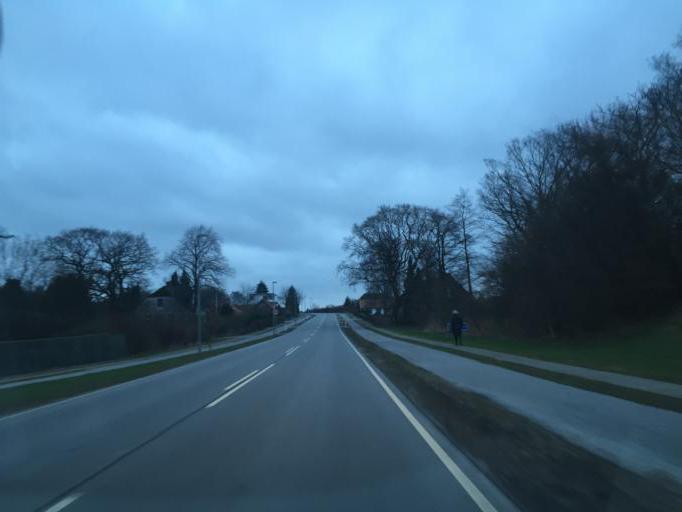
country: DK
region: South Denmark
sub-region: Haderslev Kommune
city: Starup
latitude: 55.2536
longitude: 9.5209
